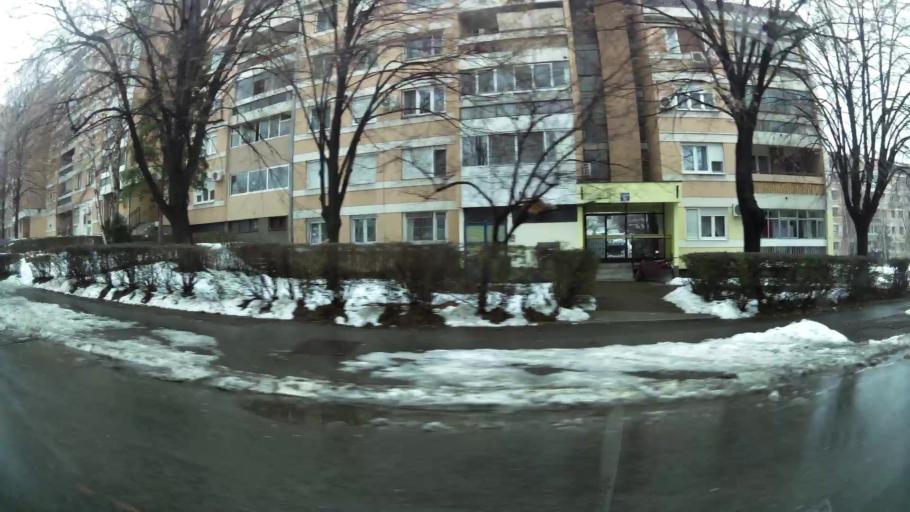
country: RS
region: Central Serbia
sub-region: Belgrade
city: Zemun
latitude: 44.8481
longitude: 20.3810
